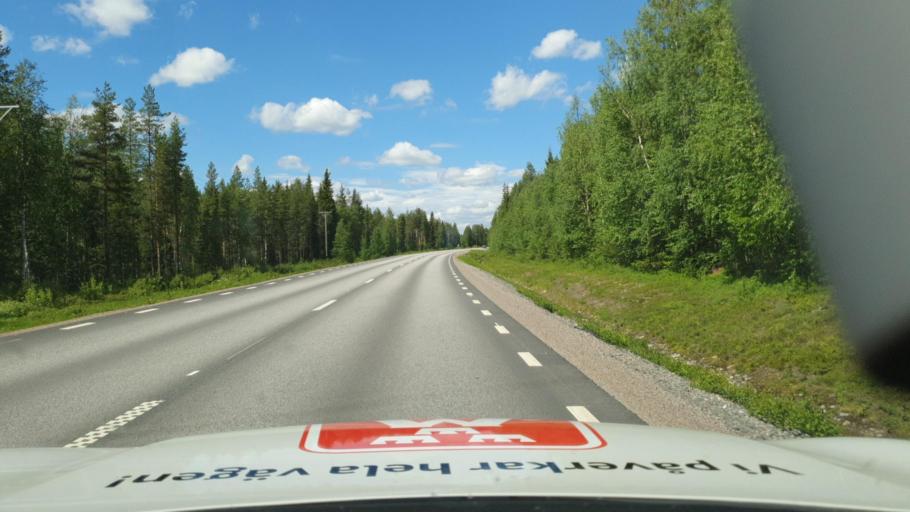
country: SE
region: Vaesterbotten
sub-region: Skelleftea Kommun
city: Langsele
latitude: 64.9423
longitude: 20.2778
